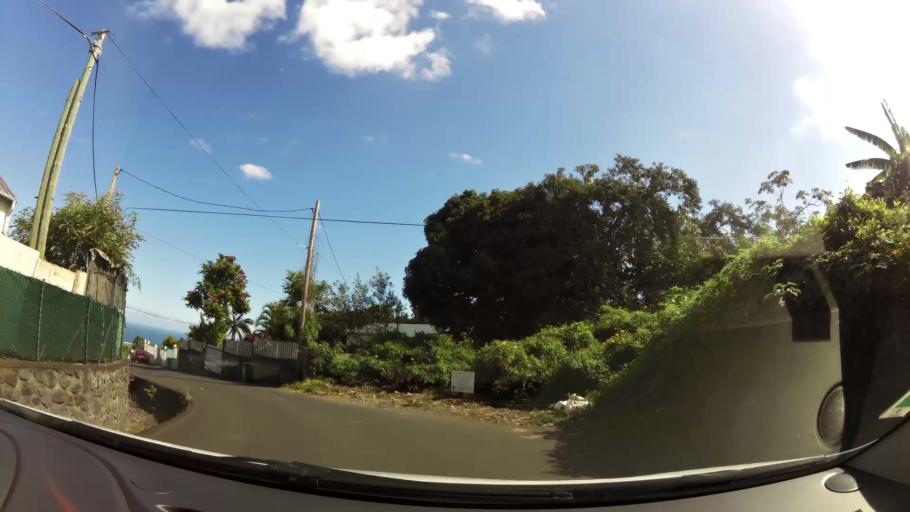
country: RE
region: Reunion
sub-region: Reunion
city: Le Tampon
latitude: -21.2889
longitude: 55.5065
